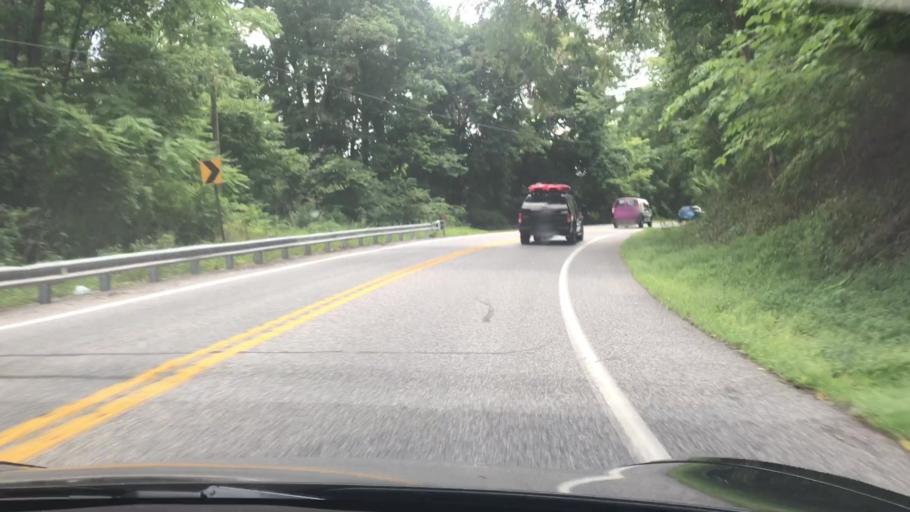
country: US
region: Pennsylvania
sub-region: York County
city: Manchester
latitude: 40.0977
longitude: -76.7610
